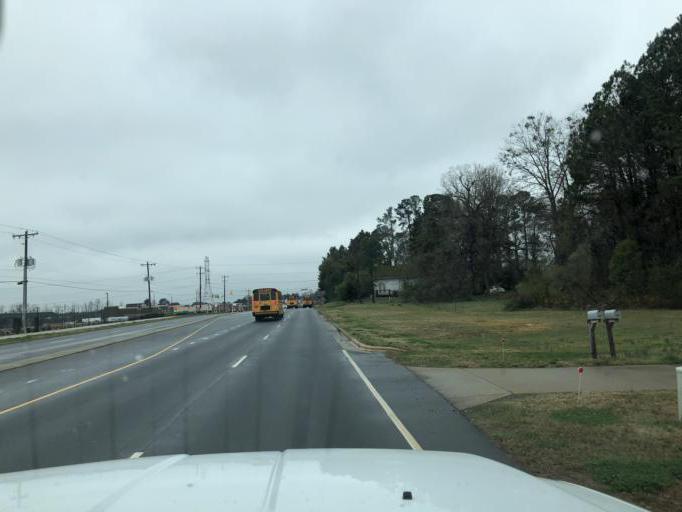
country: US
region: North Carolina
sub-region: Gaston County
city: Mount Holly
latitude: 35.3291
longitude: -80.9419
